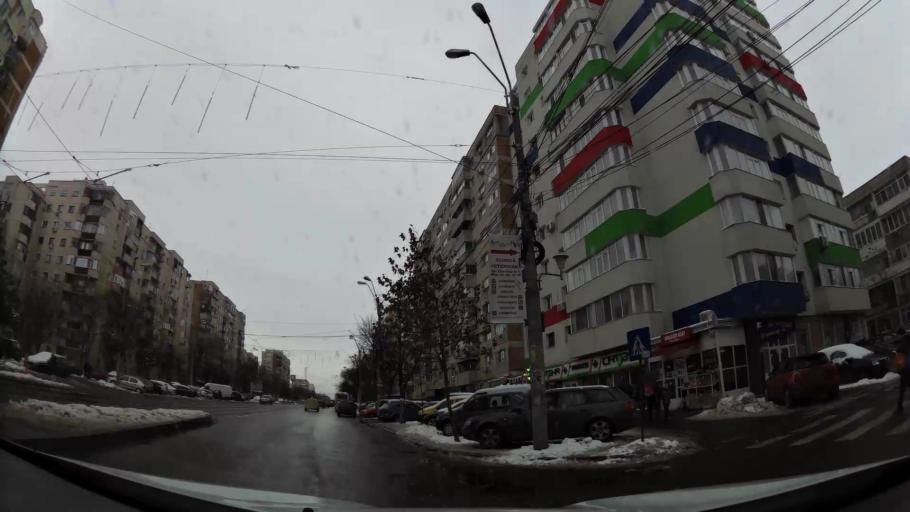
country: RO
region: Ilfov
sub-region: Comuna Popesti-Leordeni
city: Popesti-Leordeni
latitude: 44.3911
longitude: 26.1276
